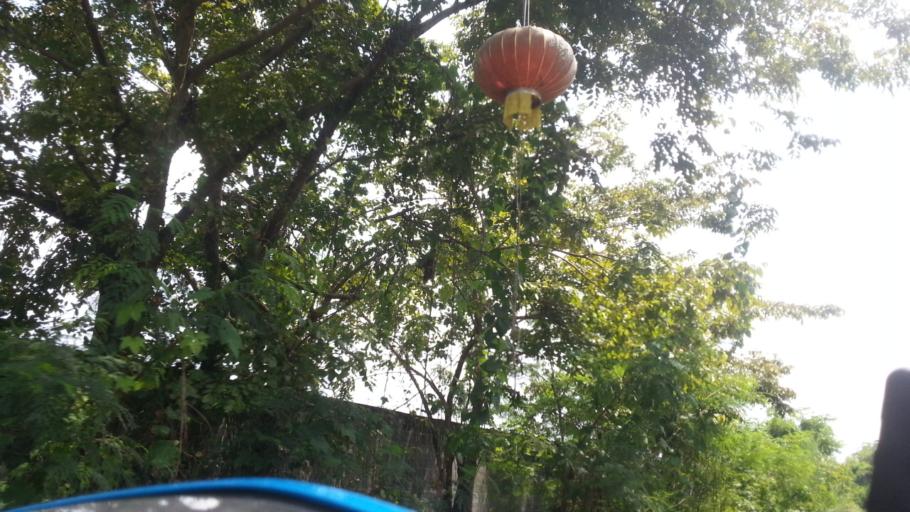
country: TH
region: Pathum Thani
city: Ban Rangsit
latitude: 14.0480
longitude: 100.8312
